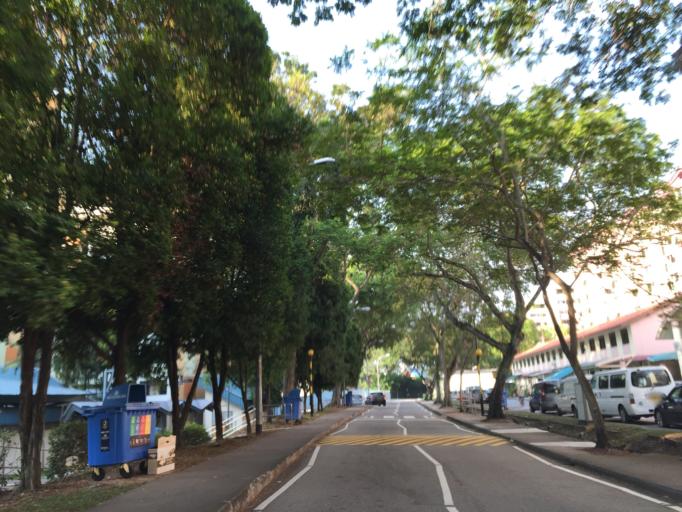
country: SG
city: Singapore
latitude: 1.2983
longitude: 103.7991
